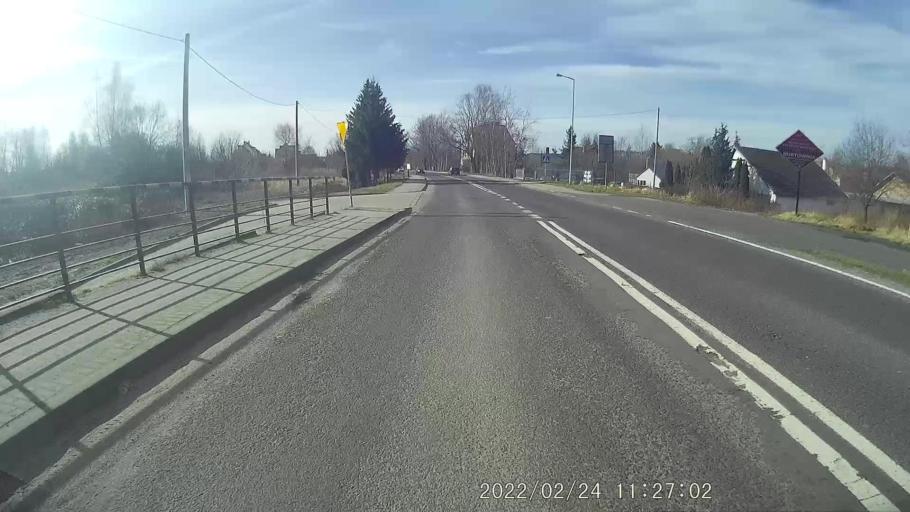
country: PL
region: Lubusz
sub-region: Powiat zaganski
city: Szprotawa
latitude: 51.5324
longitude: 15.6498
